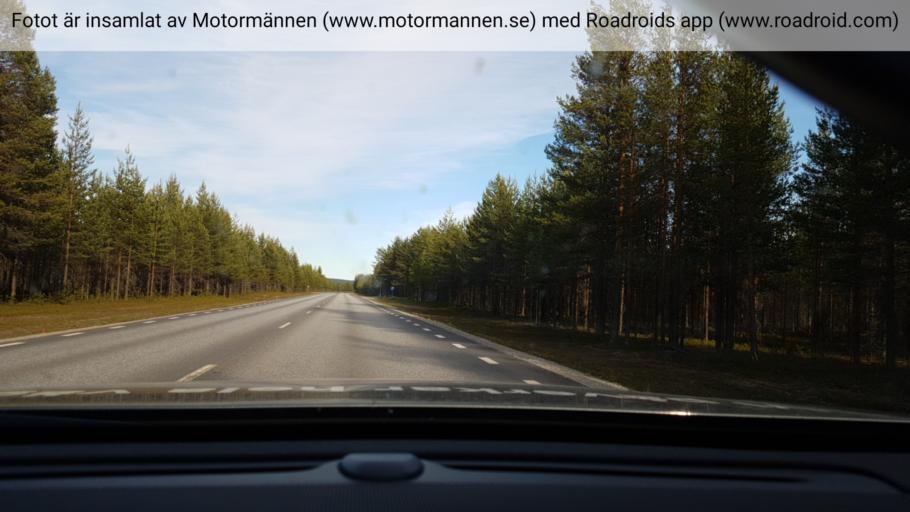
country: SE
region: Vaesterbotten
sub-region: Vindelns Kommun
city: Vindeln
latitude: 64.1626
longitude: 19.8165
